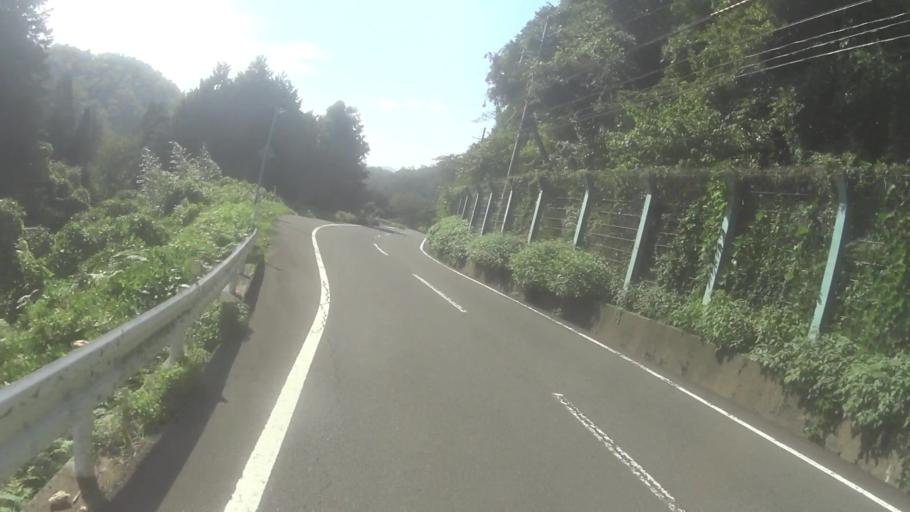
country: JP
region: Kyoto
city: Miyazu
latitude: 35.6898
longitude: 135.1215
